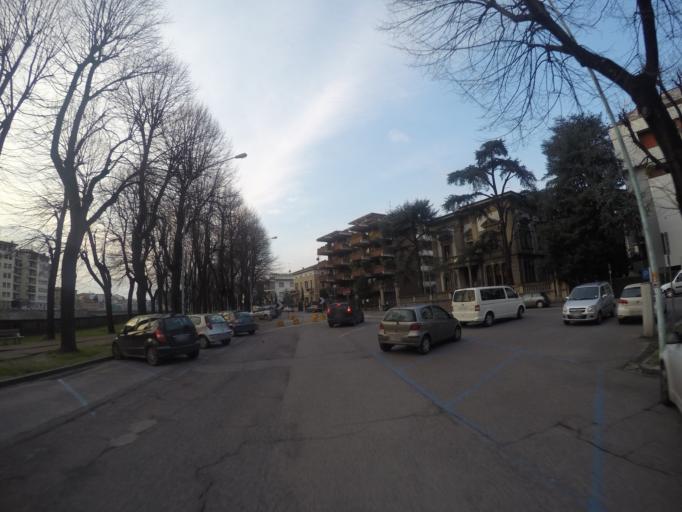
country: IT
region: Tuscany
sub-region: Provincia di Prato
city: Prato
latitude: 43.8783
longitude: 11.1066
